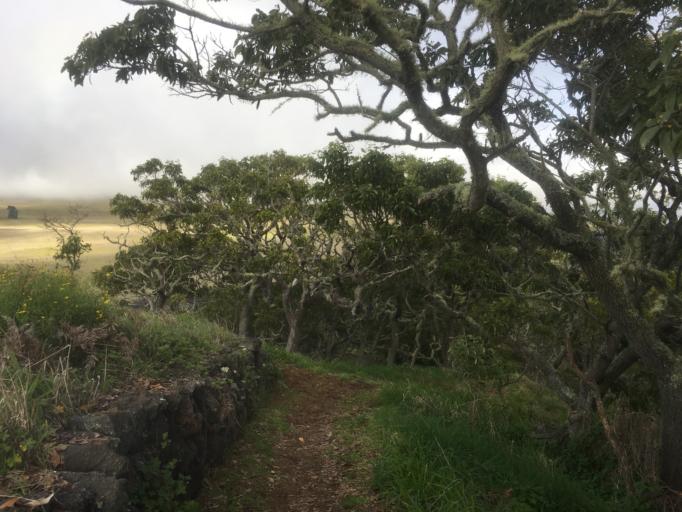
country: US
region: Hawaii
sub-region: Hawaii County
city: Volcano
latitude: 19.6874
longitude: -155.4661
